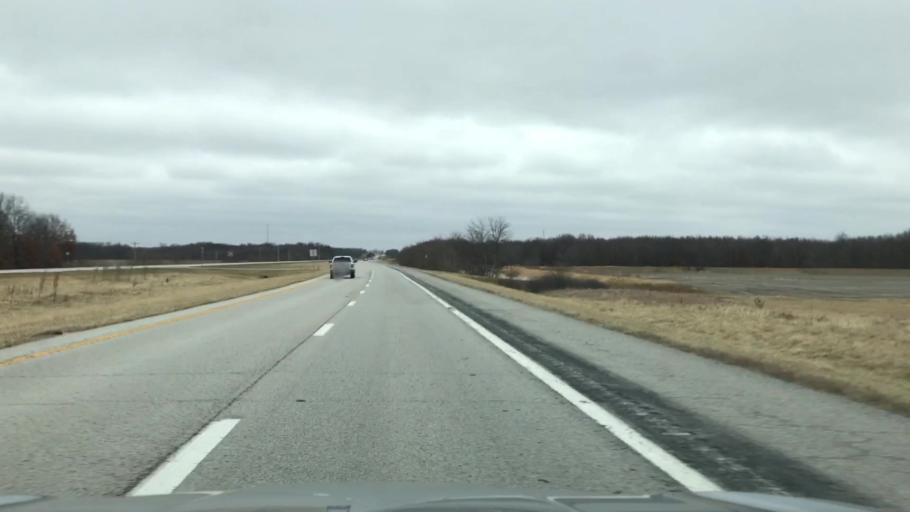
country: US
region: Missouri
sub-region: Linn County
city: Linneus
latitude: 39.7773
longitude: -93.3364
